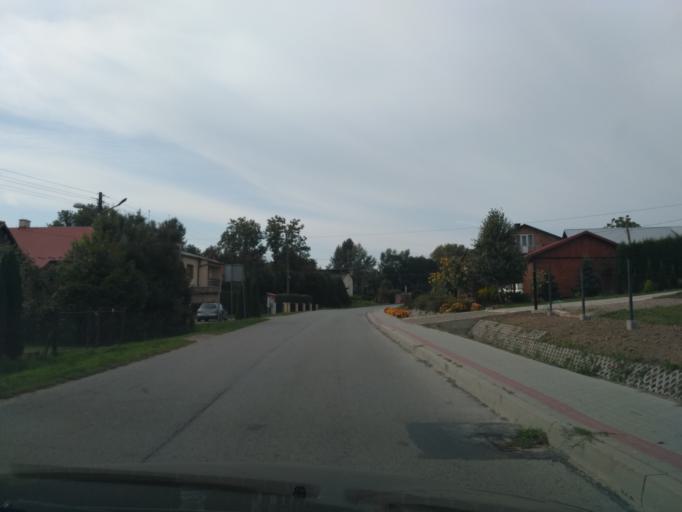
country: PL
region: Subcarpathian Voivodeship
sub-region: Powiat rzeszowski
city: Zglobien
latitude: 50.0381
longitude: 21.8378
